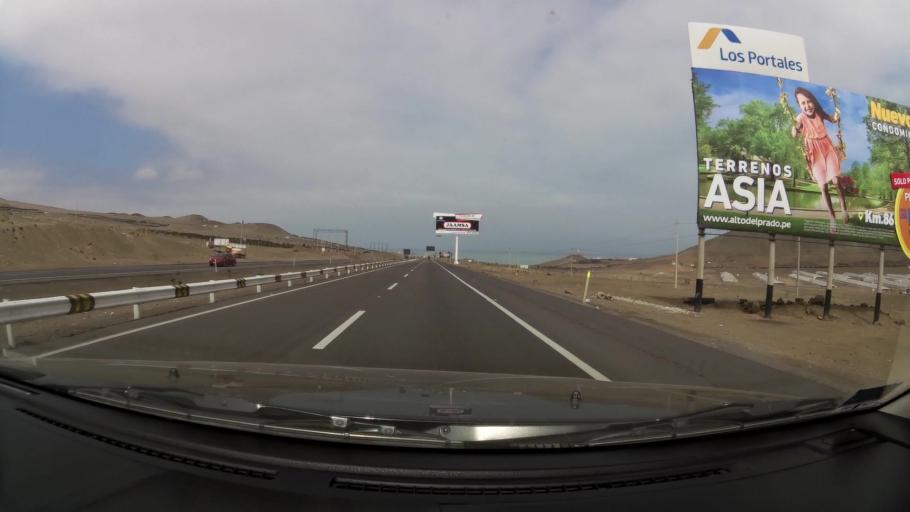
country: PE
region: Lima
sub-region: Provincia de Canete
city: Mala
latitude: -12.6134
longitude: -76.6676
